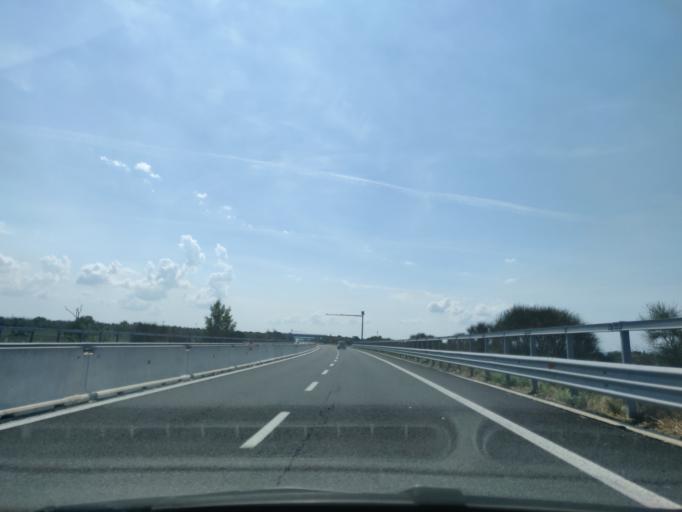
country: IT
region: Latium
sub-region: Provincia di Viterbo
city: Blera
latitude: 42.3493
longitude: 11.9811
